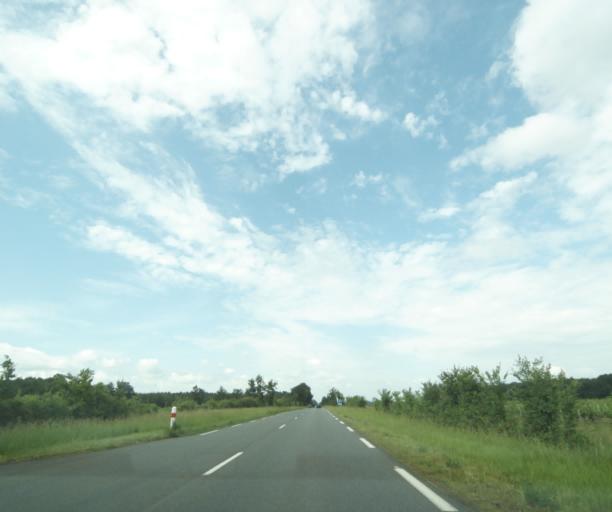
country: FR
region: Pays de la Loire
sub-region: Departement de Maine-et-Loire
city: Montreuil-Bellay
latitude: 47.1546
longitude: -0.1469
